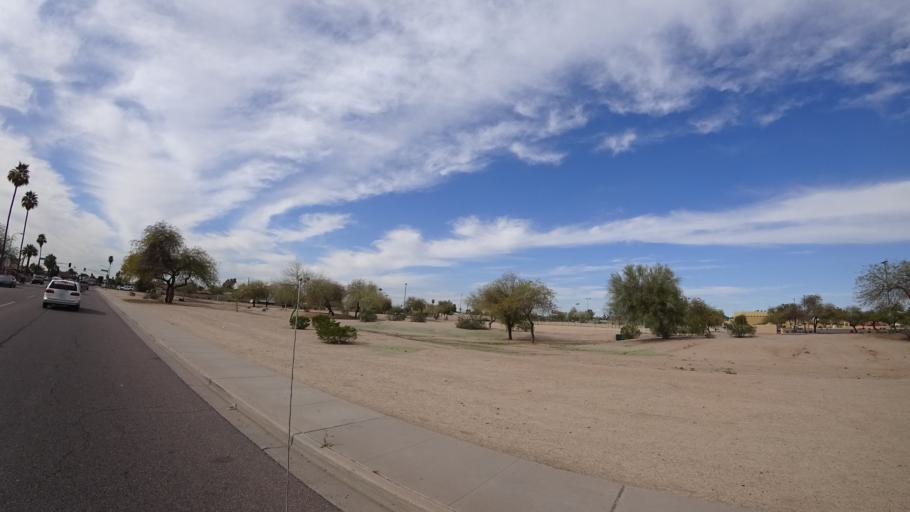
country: US
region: Arizona
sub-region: Maricopa County
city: Tolleson
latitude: 33.4731
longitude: -112.2016
